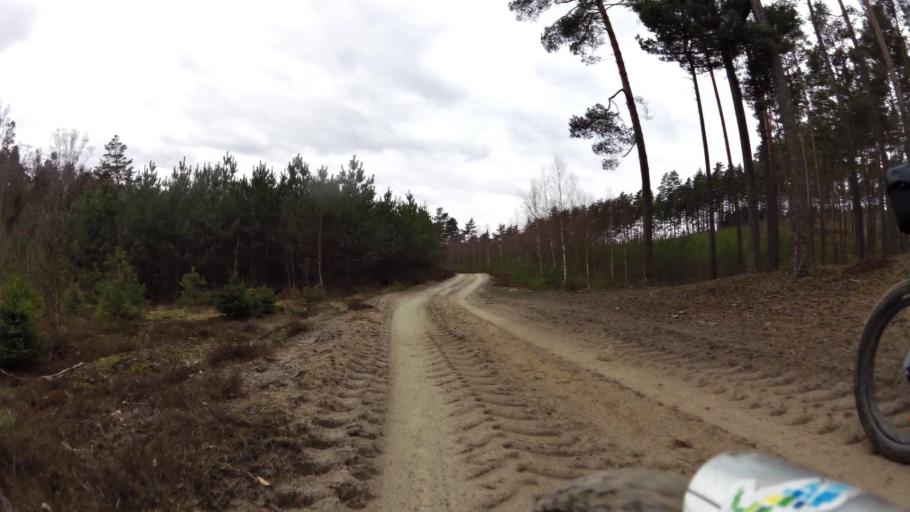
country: PL
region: Pomeranian Voivodeship
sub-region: Powiat bytowski
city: Trzebielino
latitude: 54.1299
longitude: 17.1374
